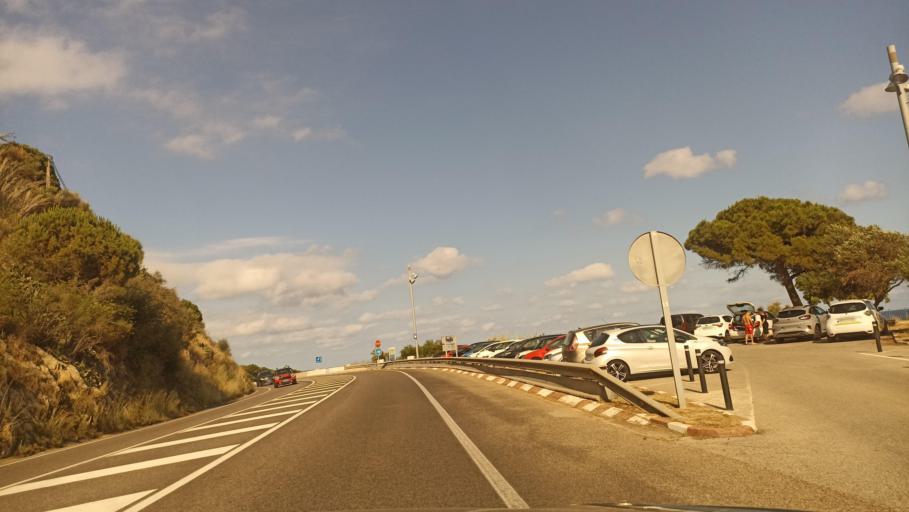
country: ES
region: Catalonia
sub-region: Provincia de Barcelona
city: Sant Pol de Mar
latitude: 41.6068
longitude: 2.6424
